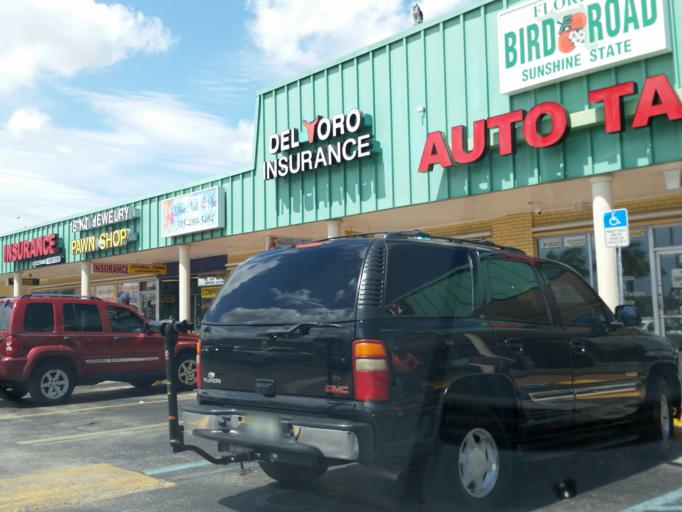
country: US
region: Florida
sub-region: Miami-Dade County
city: Olympia Heights
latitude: 25.7321
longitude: -80.3341
